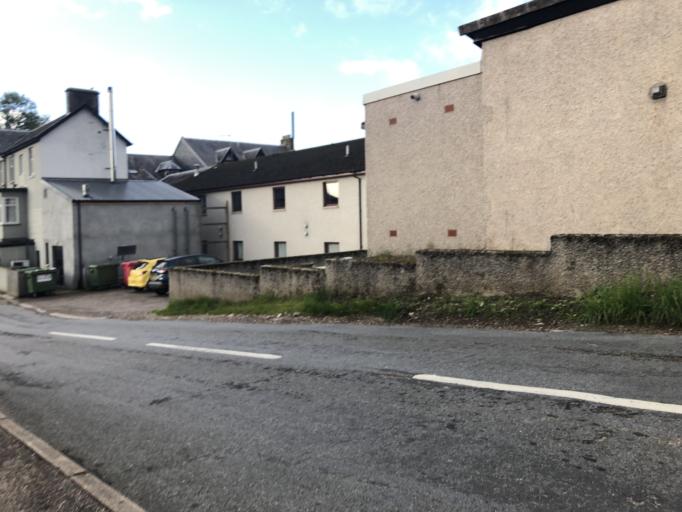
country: GB
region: Scotland
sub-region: Highland
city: Kingussie
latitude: 57.0677
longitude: -4.1165
